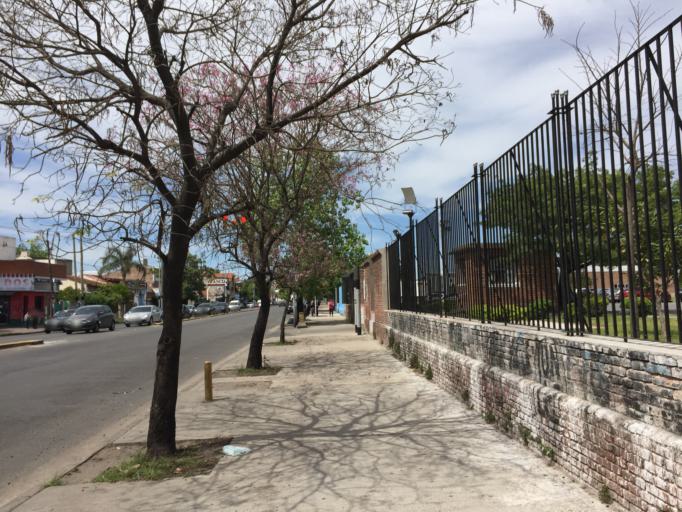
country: AR
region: Buenos Aires
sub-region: Partido de Lomas de Zamora
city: Lomas de Zamora
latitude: -34.7338
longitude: -58.3903
